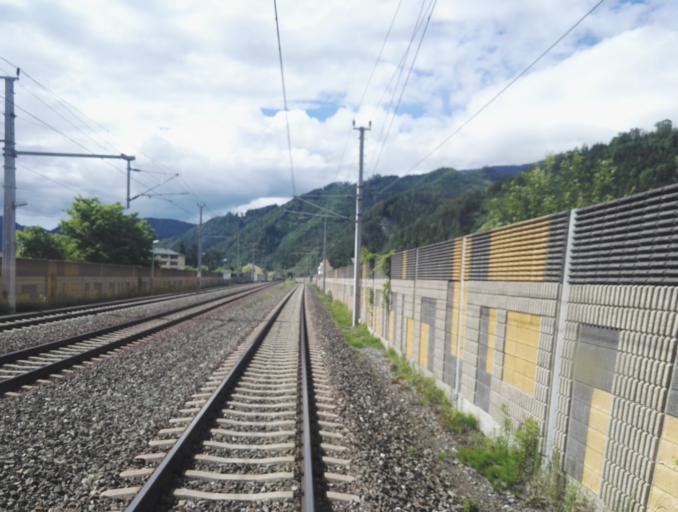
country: AT
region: Styria
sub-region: Politischer Bezirk Bruck-Muerzzuschlag
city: Pernegg an der Mur
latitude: 47.3572
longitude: 15.3447
